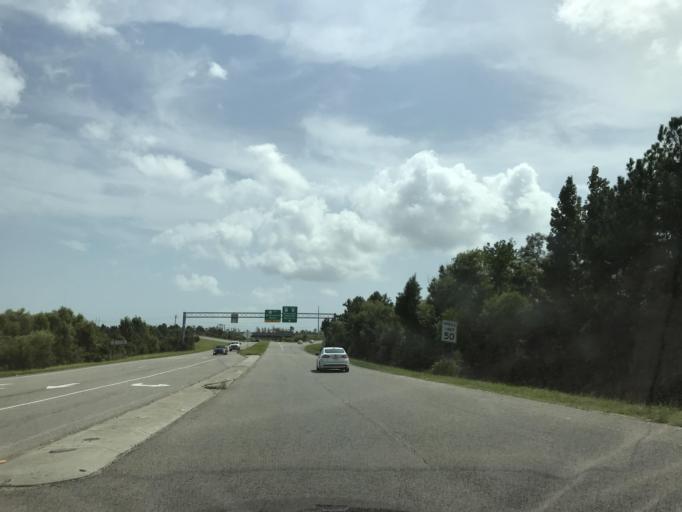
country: US
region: North Carolina
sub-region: New Hanover County
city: Wrightsboro
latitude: 34.2655
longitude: -77.9304
